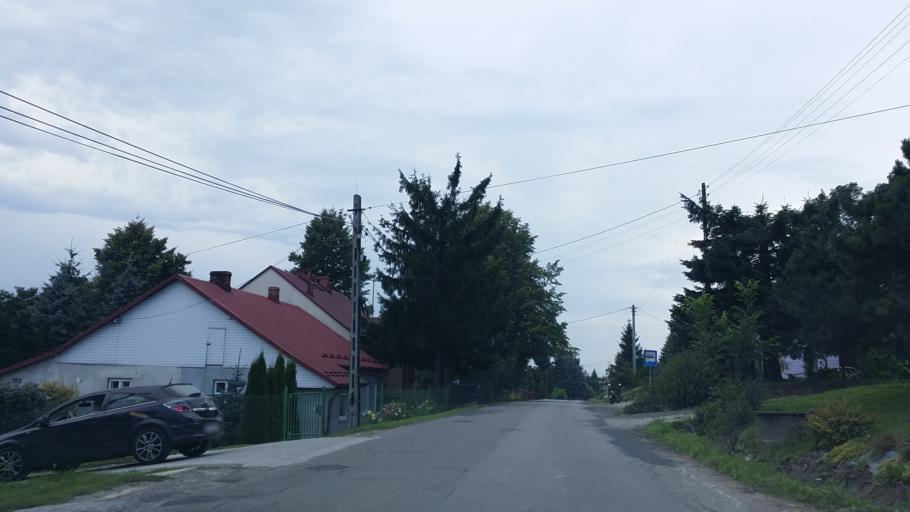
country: PL
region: Lesser Poland Voivodeship
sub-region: Powiat wielicki
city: Pawlikowice
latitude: 49.9746
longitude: 20.0220
